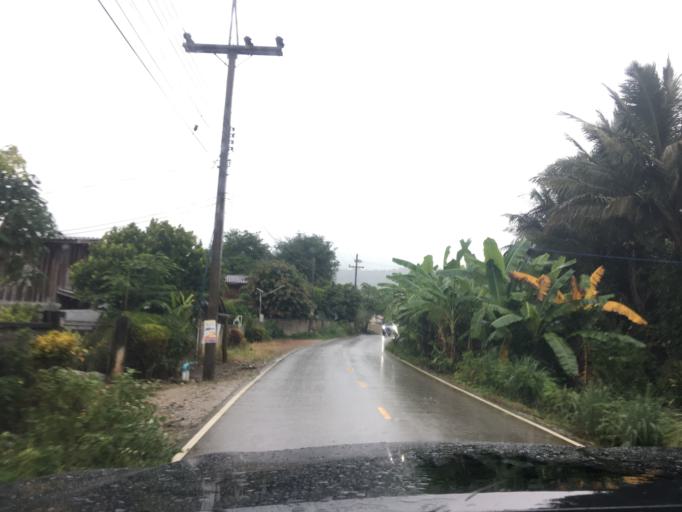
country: TH
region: Chiang Rai
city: Chiang Khong
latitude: 20.3009
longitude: 100.2518
